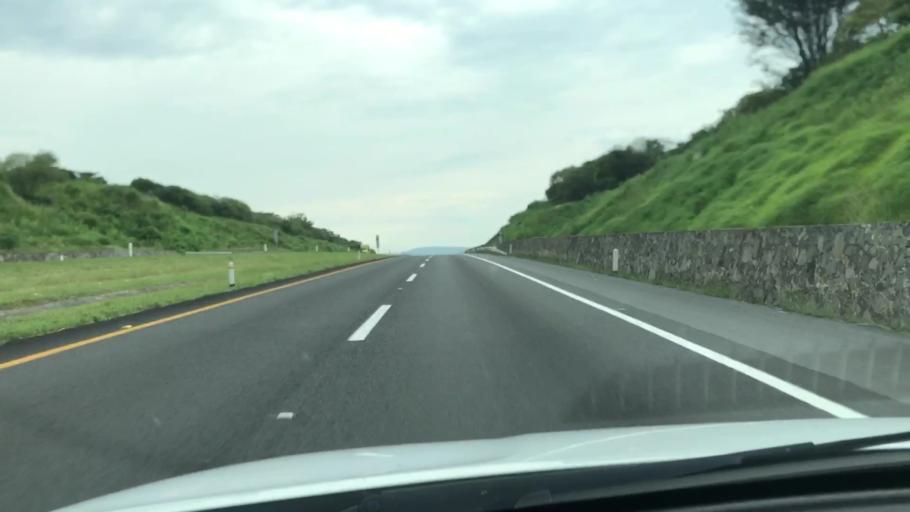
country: MX
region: Jalisco
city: Ocotlan
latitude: 20.4219
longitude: -102.7633
